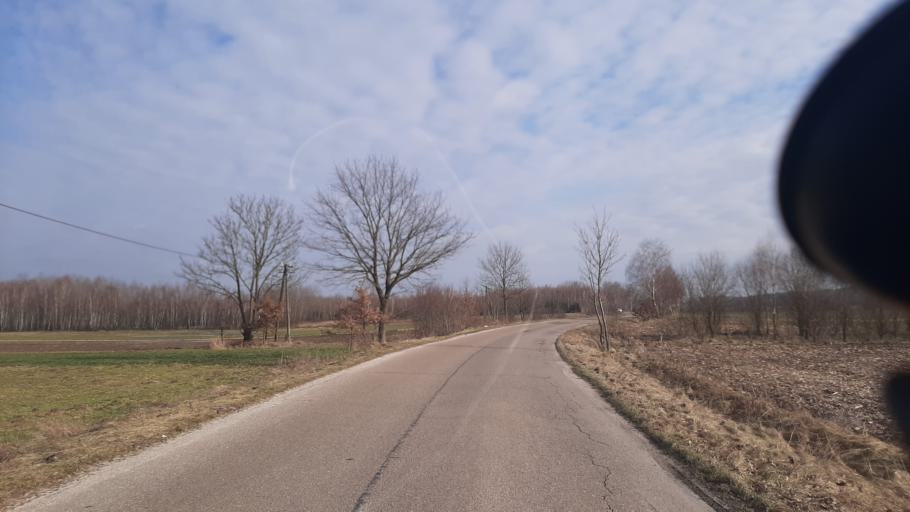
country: PL
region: Lublin Voivodeship
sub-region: Powiat lubartowski
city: Uscimow Stary
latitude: 51.4699
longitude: 22.9722
